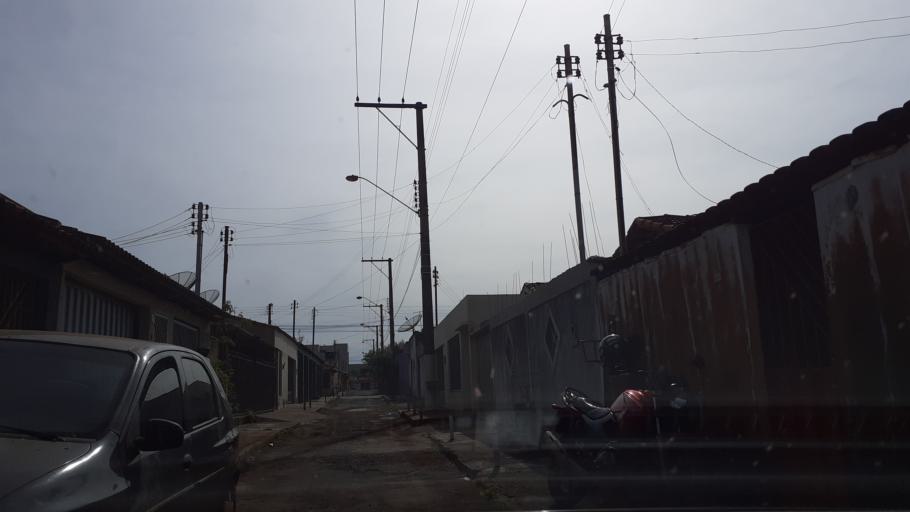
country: BR
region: Goias
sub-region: Itumbiara
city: Itumbiara
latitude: -18.4169
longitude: -49.2374
